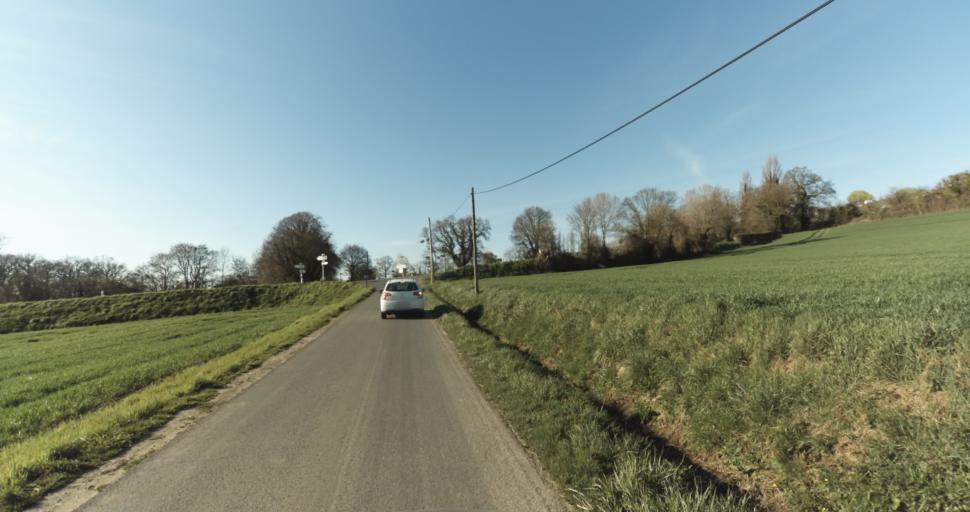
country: FR
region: Lower Normandy
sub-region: Departement du Calvados
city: Saint-Pierre-sur-Dives
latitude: 49.0439
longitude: 0.0293
